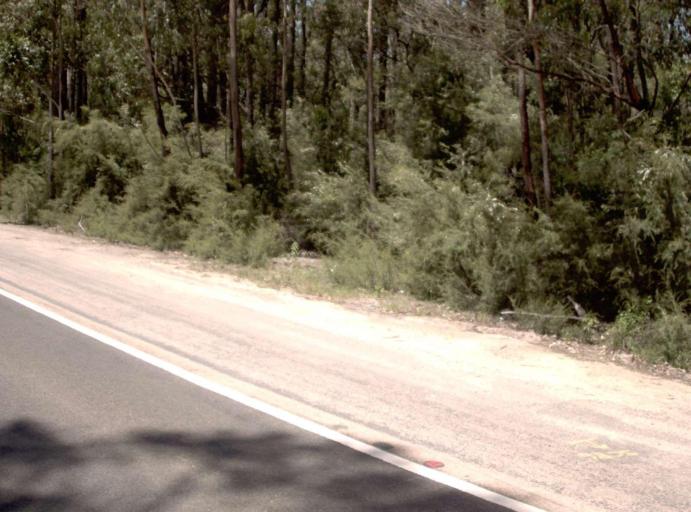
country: AU
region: Victoria
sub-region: East Gippsland
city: Lakes Entrance
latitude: -37.7017
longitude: 148.5843
